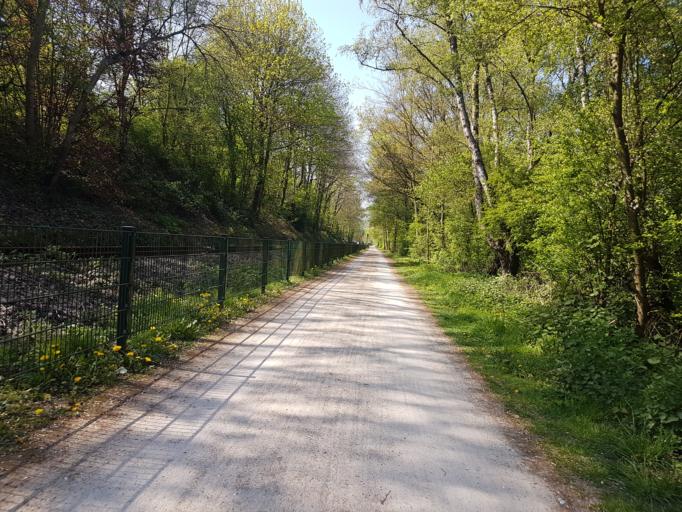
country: DE
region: North Rhine-Westphalia
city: Witten
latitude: 51.4266
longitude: 7.3328
